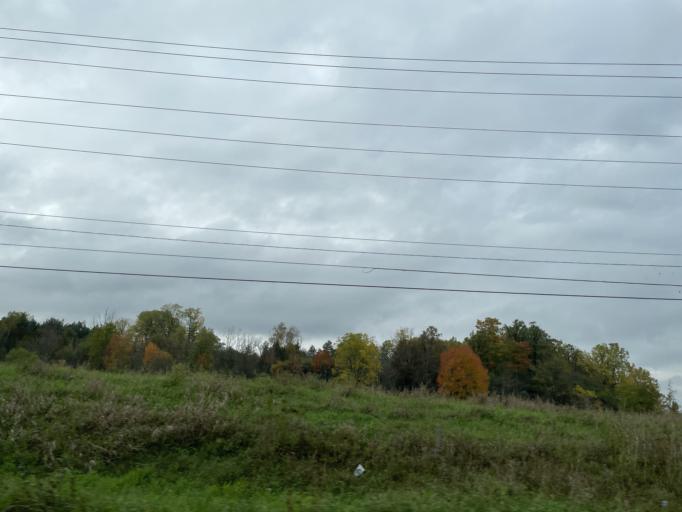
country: CA
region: Ontario
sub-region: Wellington County
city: Guelph
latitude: 43.5486
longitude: -80.1958
